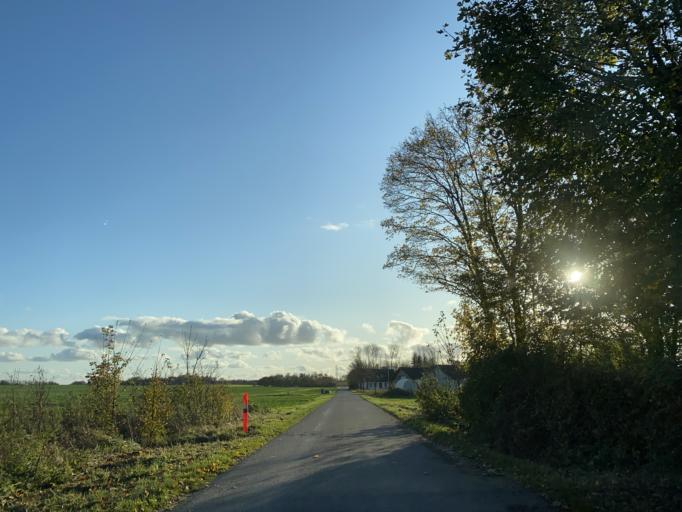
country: DK
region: Central Jutland
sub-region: Viborg Kommune
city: Bjerringbro
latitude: 56.3234
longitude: 9.7032
